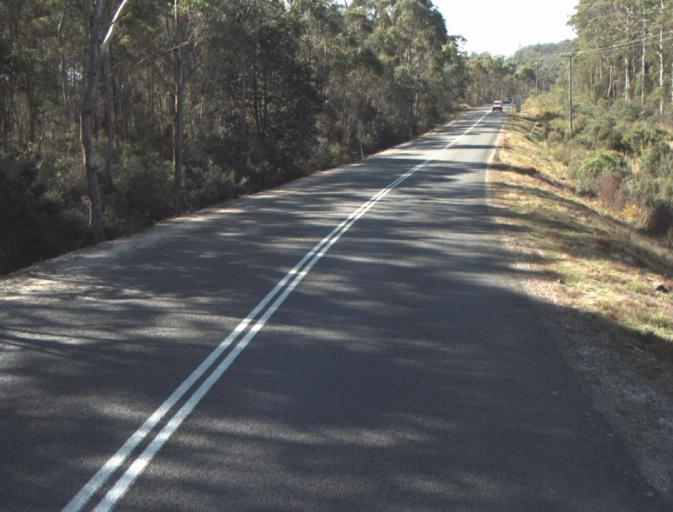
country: AU
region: Tasmania
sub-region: Launceston
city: Mayfield
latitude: -41.3307
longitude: 147.1798
